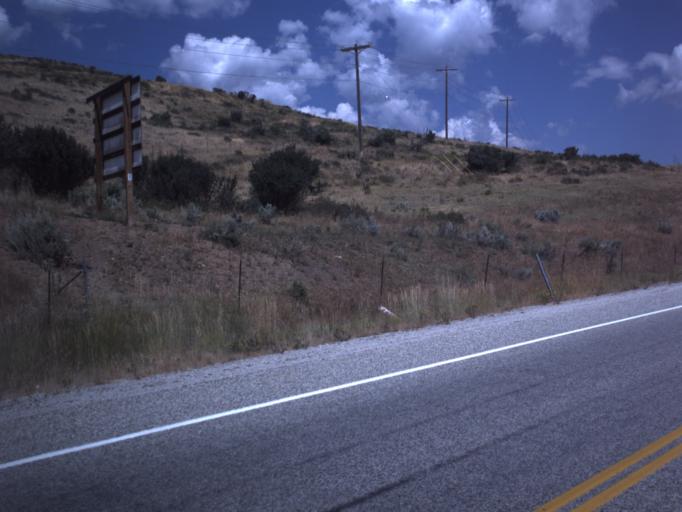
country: US
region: Idaho
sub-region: Bear Lake County
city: Paris
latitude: 41.9421
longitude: -111.4098
